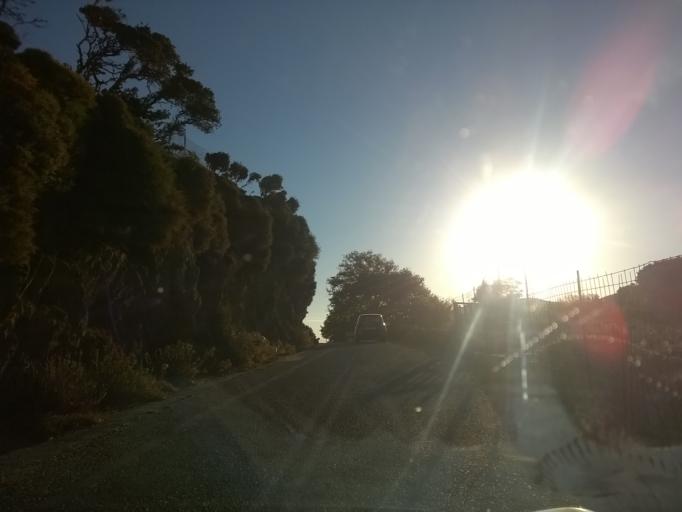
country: GR
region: South Aegean
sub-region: Nomos Kykladon
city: Filotion
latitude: 37.0448
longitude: 25.5064
